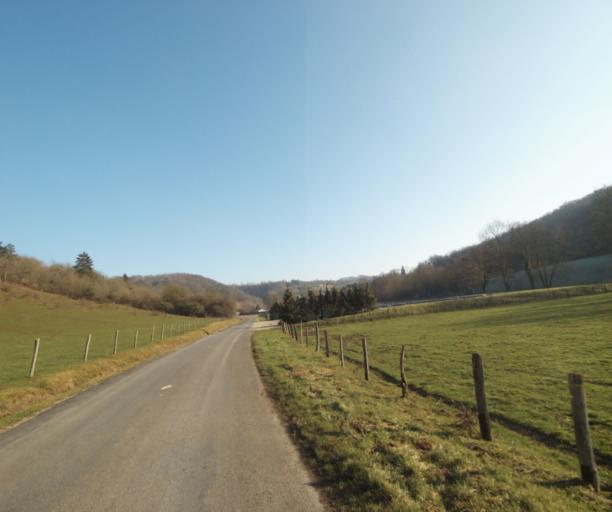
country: FR
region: Champagne-Ardenne
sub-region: Departement de la Haute-Marne
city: Chevillon
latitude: 48.5008
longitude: 5.1833
